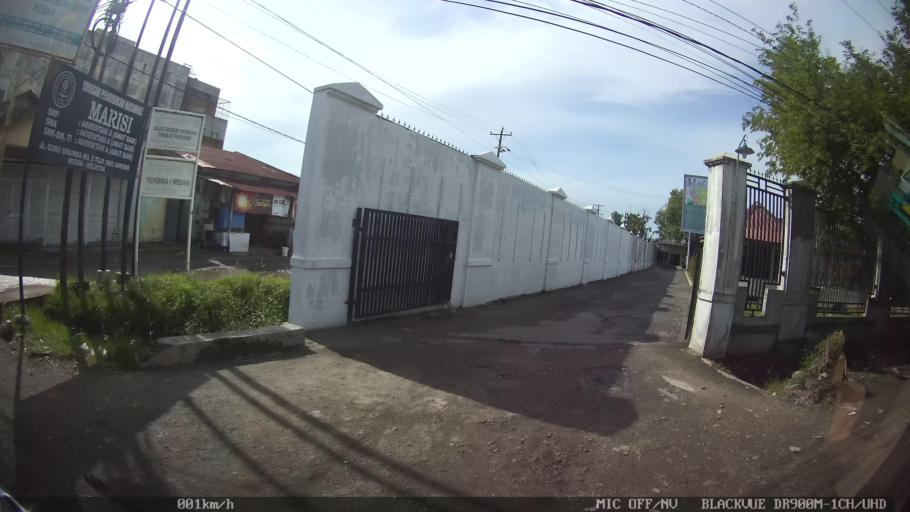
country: ID
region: North Sumatra
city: Medan
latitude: 3.6233
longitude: 98.6606
